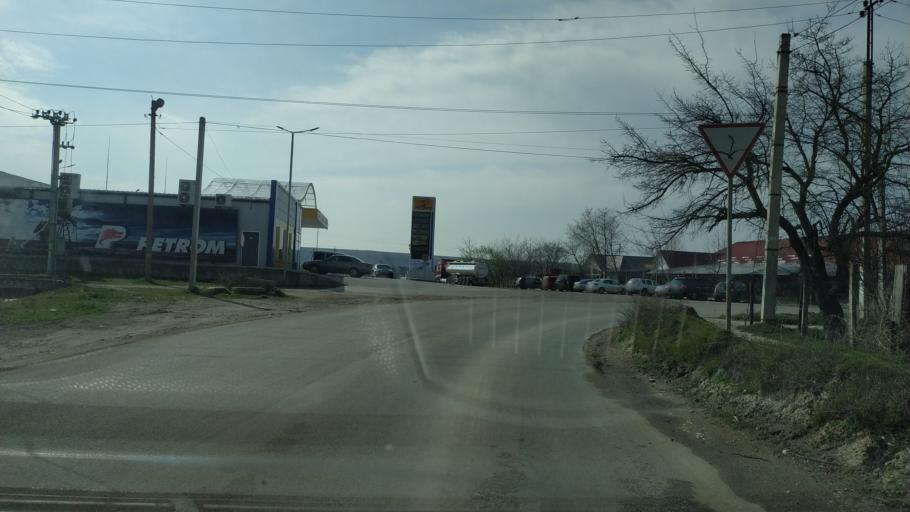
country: MD
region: Gagauzia
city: Vulcanesti
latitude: 45.6773
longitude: 28.4119
